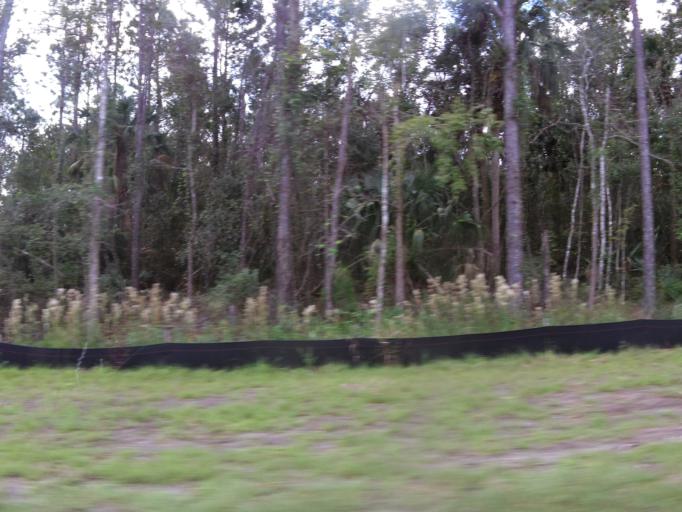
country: US
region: Florida
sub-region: Saint Johns County
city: Villano Beach
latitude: 30.0032
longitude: -81.4005
